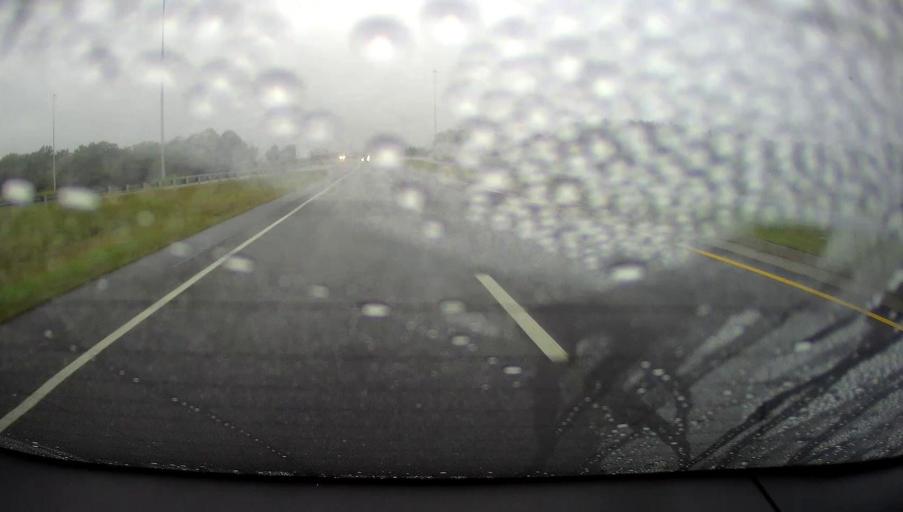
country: US
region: Georgia
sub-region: Houston County
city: Robins Air Force Base
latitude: 32.5521
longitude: -83.5952
